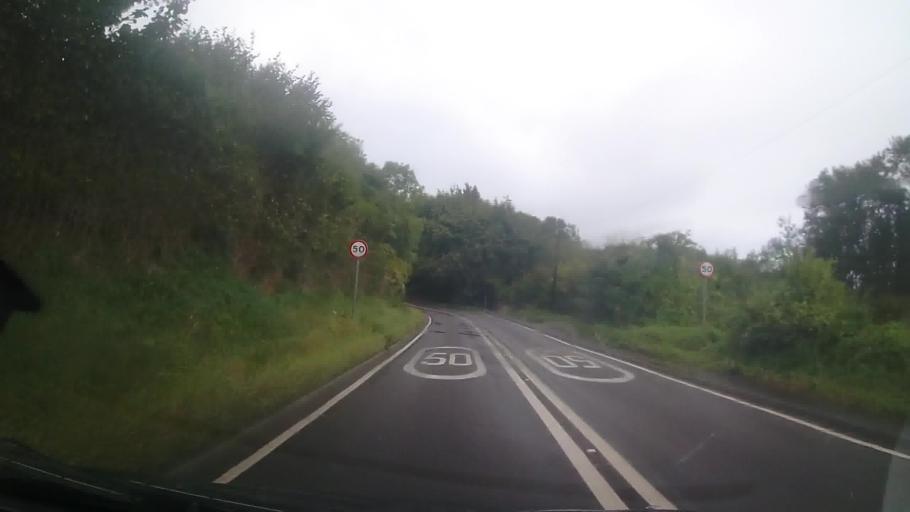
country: GB
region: England
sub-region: Shropshire
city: Much Wenlock
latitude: 52.6096
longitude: -2.5460
